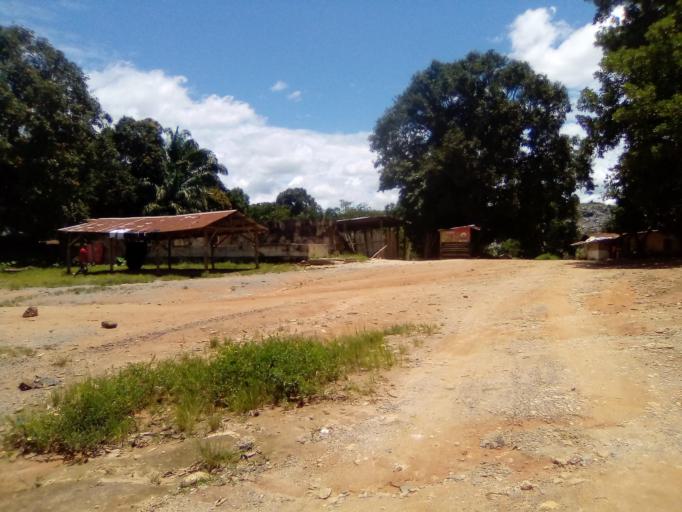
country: SL
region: Eastern Province
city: Koidu
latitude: 8.6370
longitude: -10.9749
